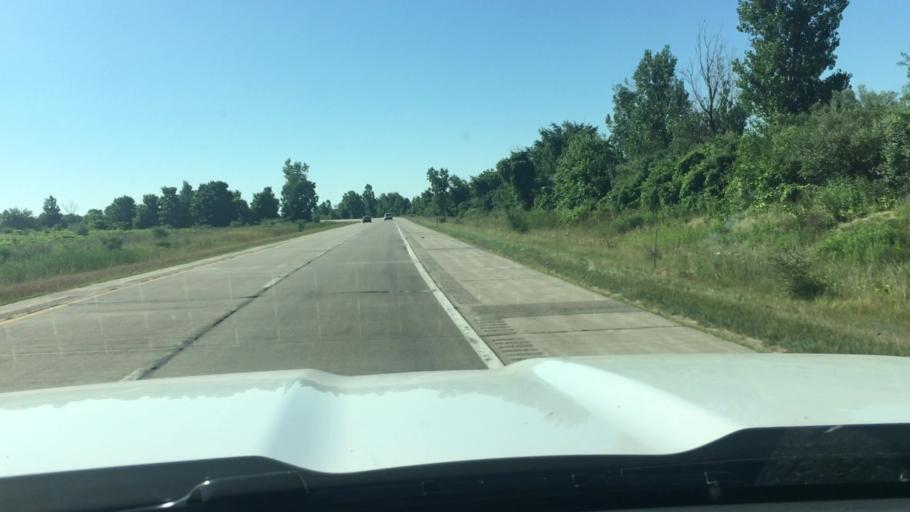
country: US
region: Michigan
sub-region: Clinton County
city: Wacousta
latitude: 42.7945
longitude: -84.6861
